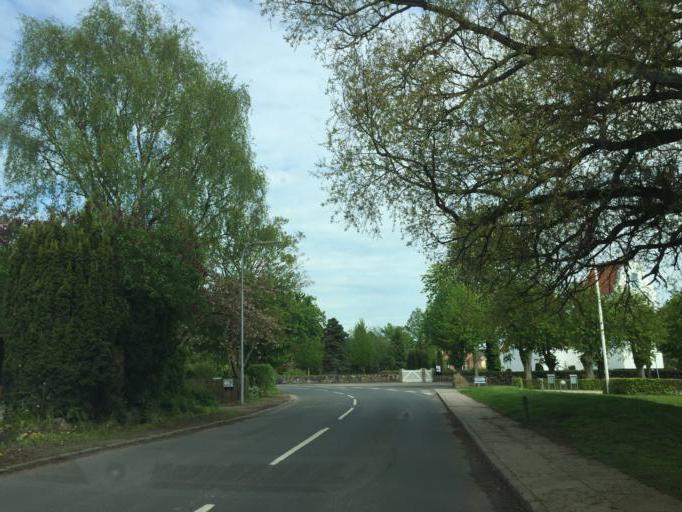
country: DK
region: South Denmark
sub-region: Odense Kommune
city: Hojby
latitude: 55.3311
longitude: 10.4418
